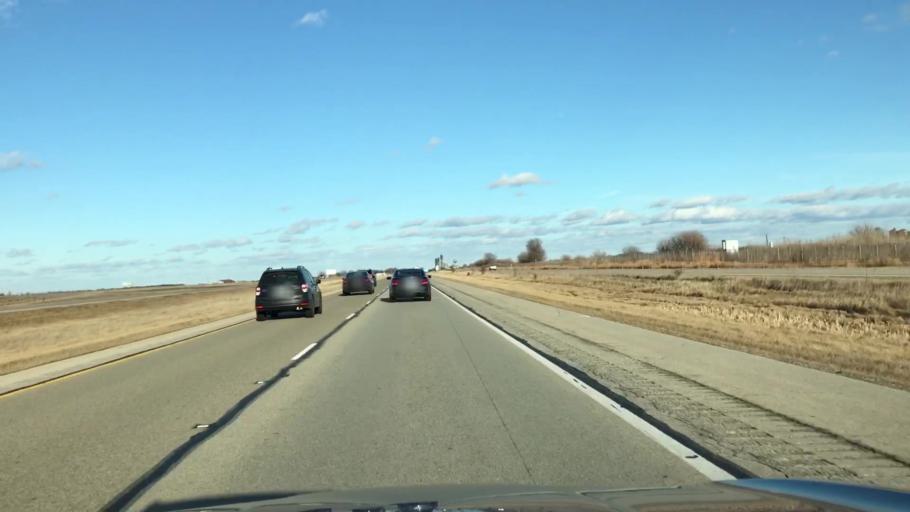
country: US
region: Illinois
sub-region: McLean County
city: Normal
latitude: 40.5500
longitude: -88.9210
